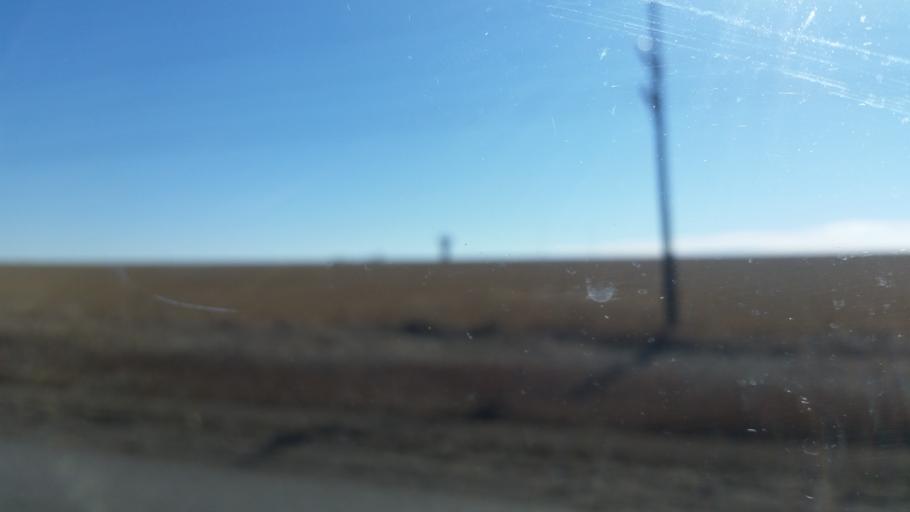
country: US
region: Colorado
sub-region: Weld County
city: Windsor
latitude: 40.4066
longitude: -104.8939
